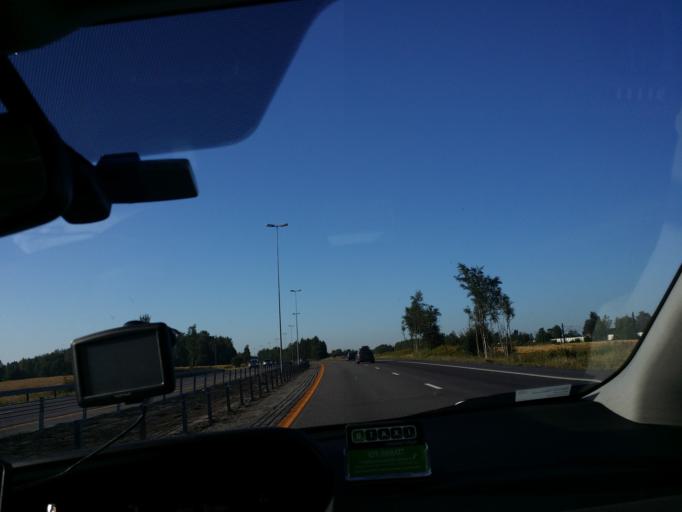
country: NO
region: Akershus
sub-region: Ullensaker
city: Klofta
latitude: 60.1023
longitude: 11.1429
